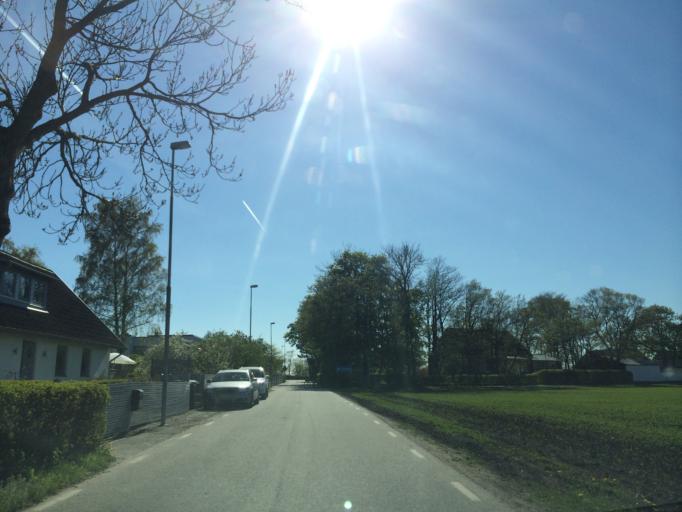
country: SE
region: Skane
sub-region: Lomma Kommun
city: Lomma
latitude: 55.6994
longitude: 13.0525
